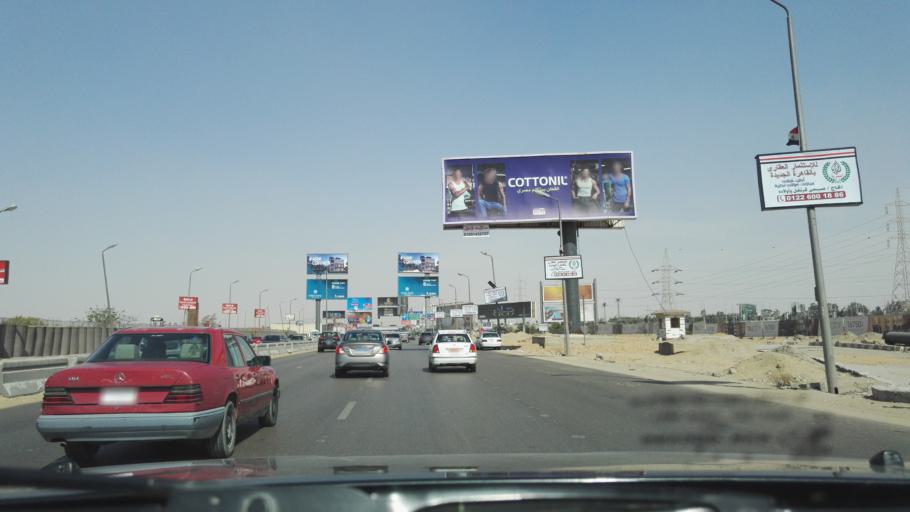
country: EG
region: Muhafazat al Qalyubiyah
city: Al Khankah
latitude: 30.0790
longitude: 31.4287
